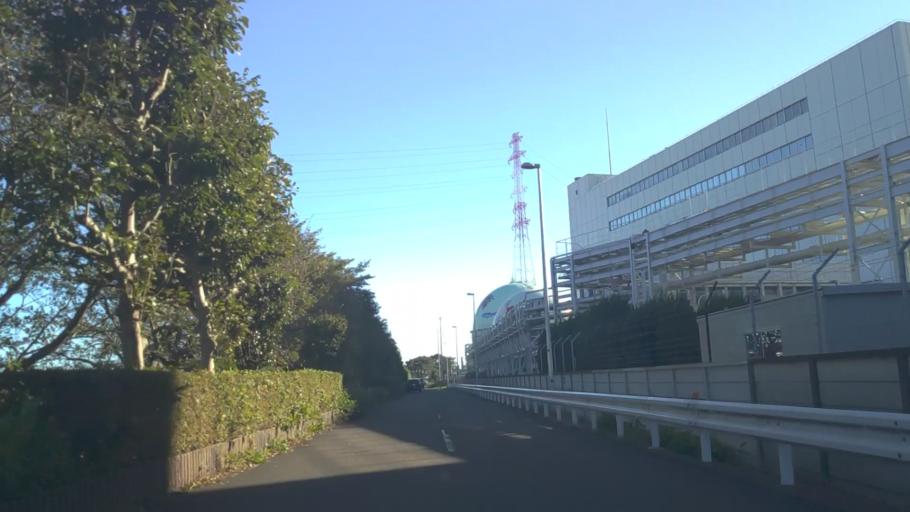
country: JP
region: Kanagawa
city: Atsugi
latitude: 35.4324
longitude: 139.3713
